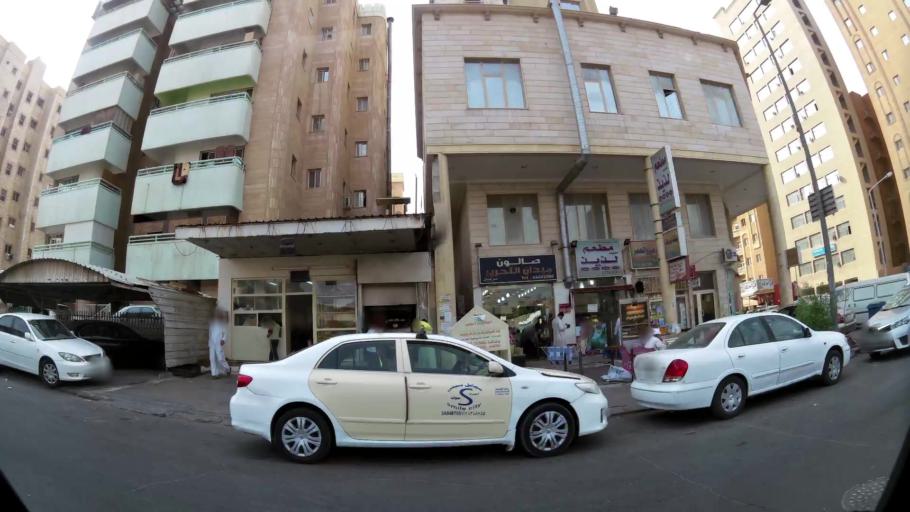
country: KW
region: Al Farwaniyah
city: Al Farwaniyah
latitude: 29.2952
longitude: 47.9741
